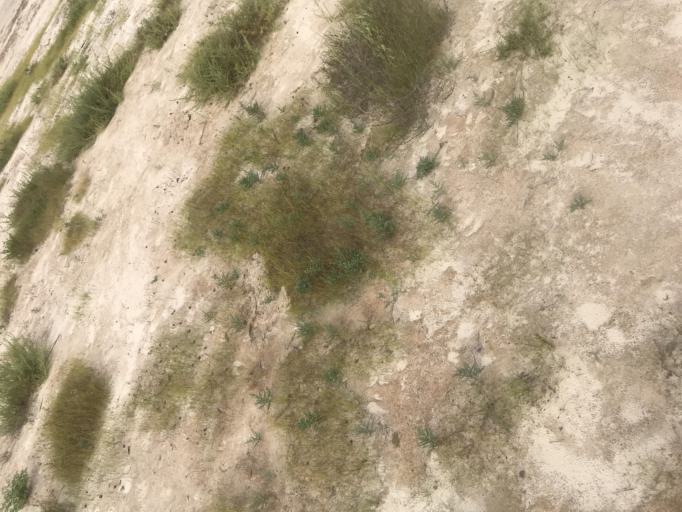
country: SN
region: Saint-Louis
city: Saint-Louis
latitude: 15.9283
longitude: -16.4665
